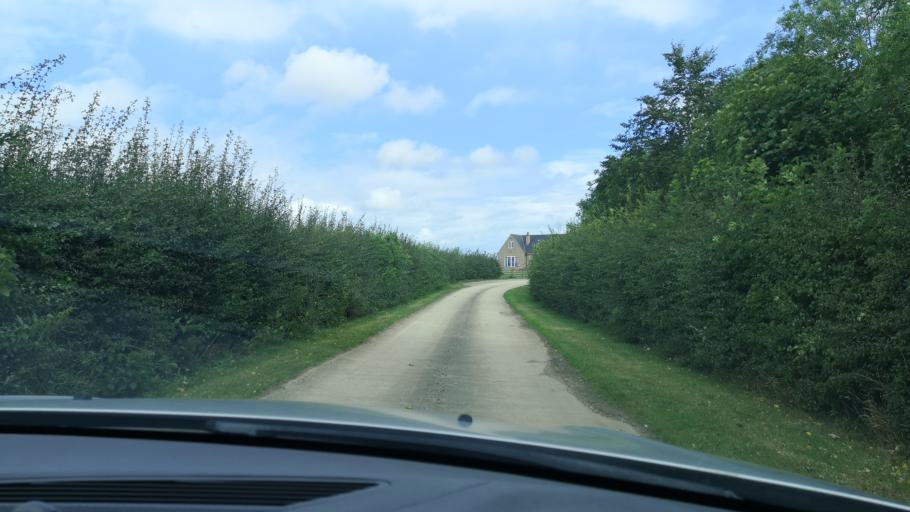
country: GB
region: England
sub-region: City and Borough of Wakefield
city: Darrington
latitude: 53.6839
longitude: -1.2587
